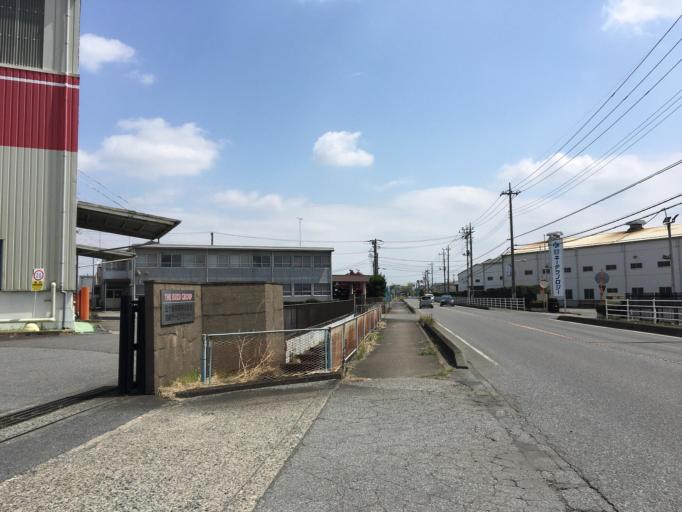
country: JP
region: Gunma
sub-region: Sawa-gun
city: Tamamura
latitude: 36.2919
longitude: 139.1445
